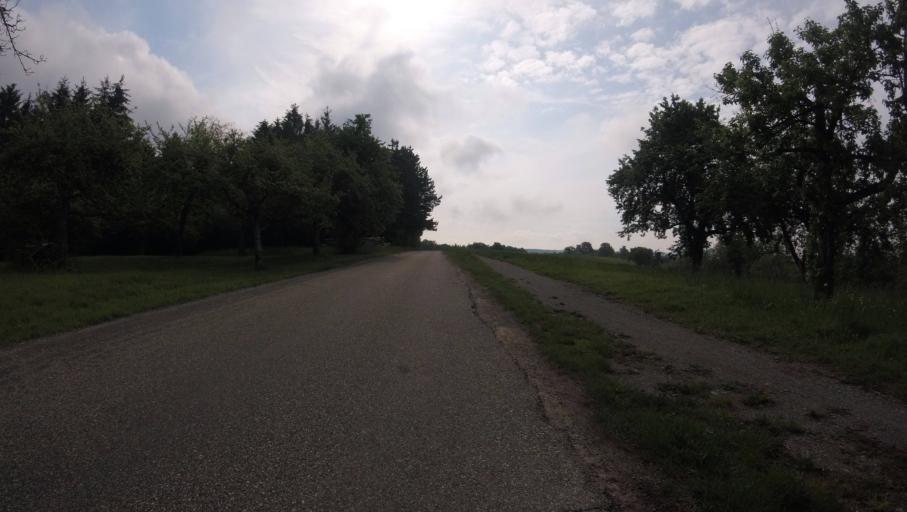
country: DE
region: Baden-Wuerttemberg
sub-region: Regierungsbezirk Stuttgart
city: Althutte
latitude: 48.9351
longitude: 9.5368
